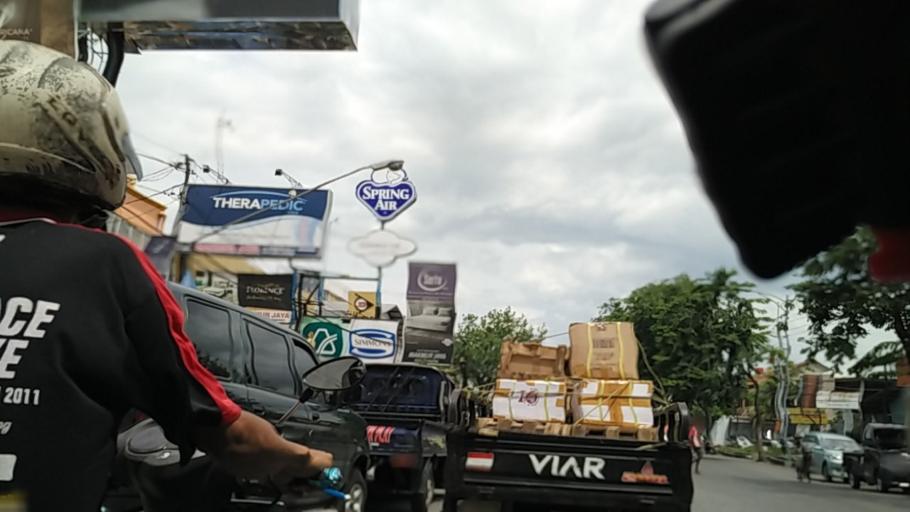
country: ID
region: Central Java
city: Semarang
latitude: -6.9697
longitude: 110.4324
